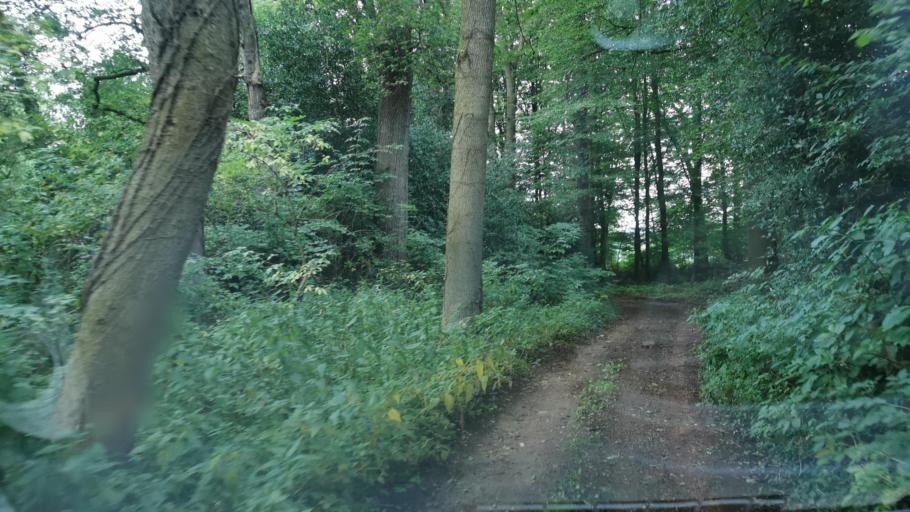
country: NL
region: Overijssel
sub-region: Gemeente Oldenzaal
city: Oldenzaal
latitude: 52.3223
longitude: 6.9475
